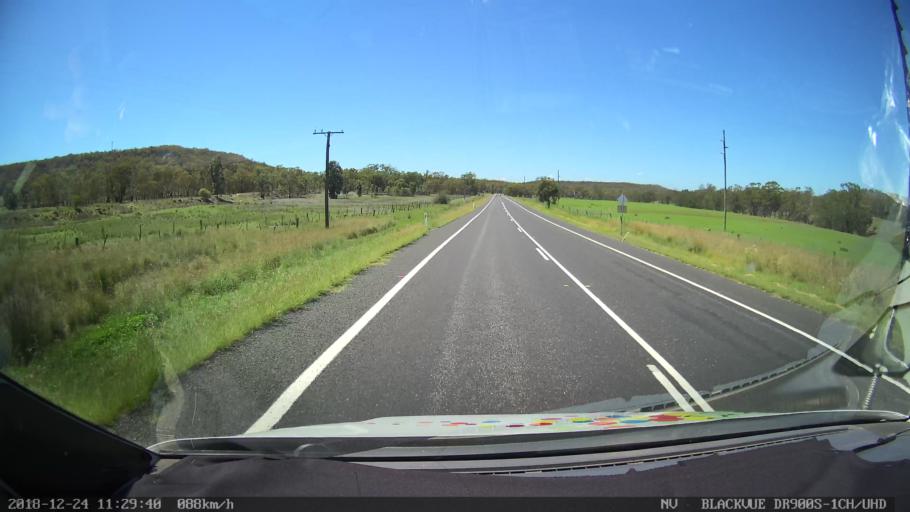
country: AU
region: New South Wales
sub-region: Upper Hunter Shire
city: Merriwa
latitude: -32.1953
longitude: 150.4641
